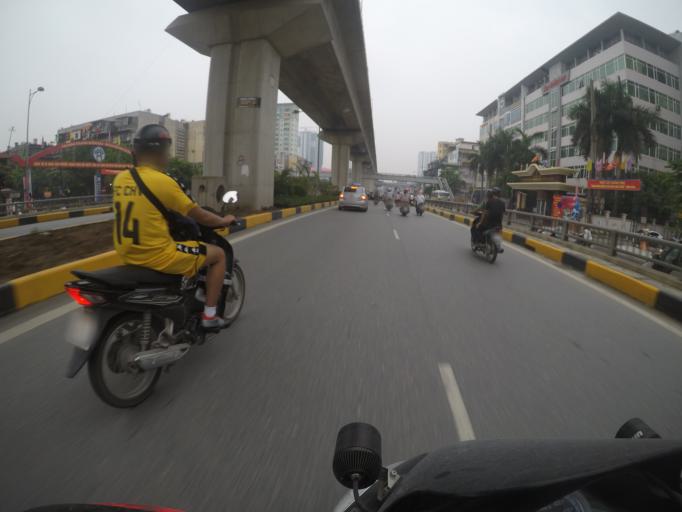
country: VN
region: Ha Noi
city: Thanh Xuan
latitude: 20.9898
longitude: 105.8011
